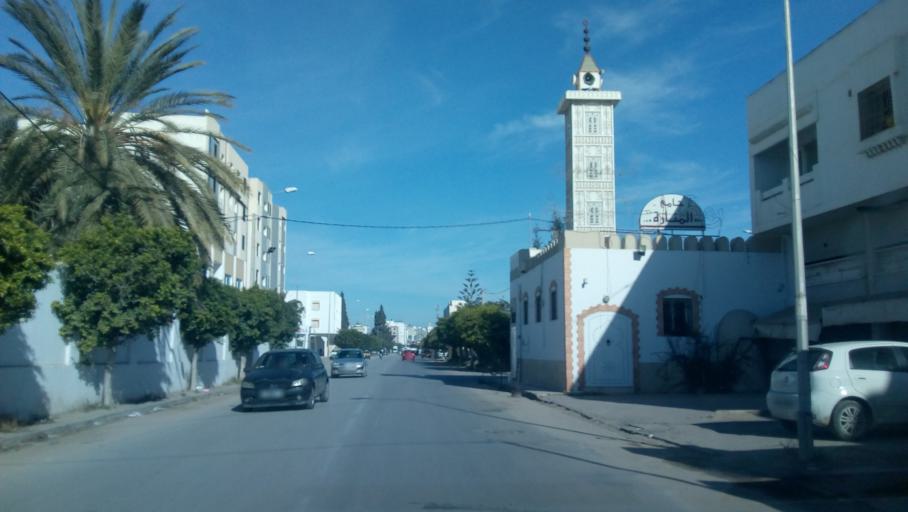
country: TN
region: Safaqis
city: Sfax
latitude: 34.7532
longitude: 10.7383
